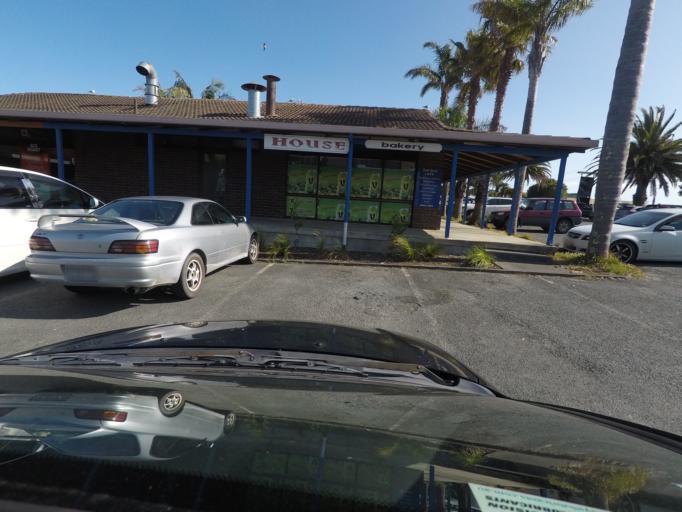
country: NZ
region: Auckland
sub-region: Auckland
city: Warkworth
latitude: -36.4203
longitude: 174.7236
